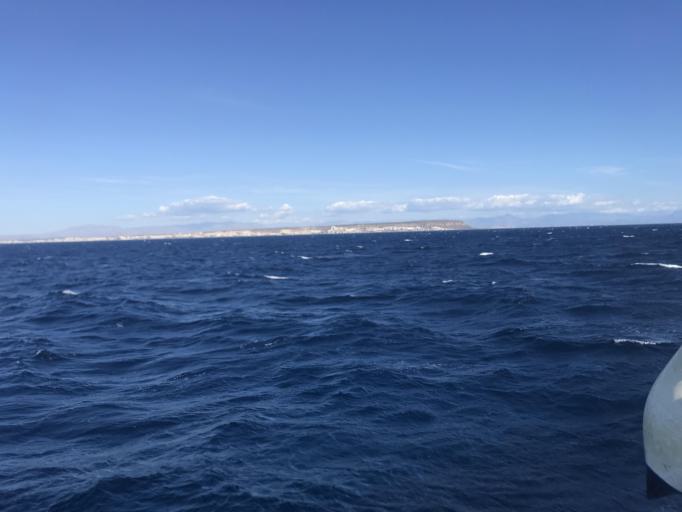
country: ES
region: Valencia
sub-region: Provincia de Alicante
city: Santa Pola
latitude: 38.1365
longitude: -0.5294
